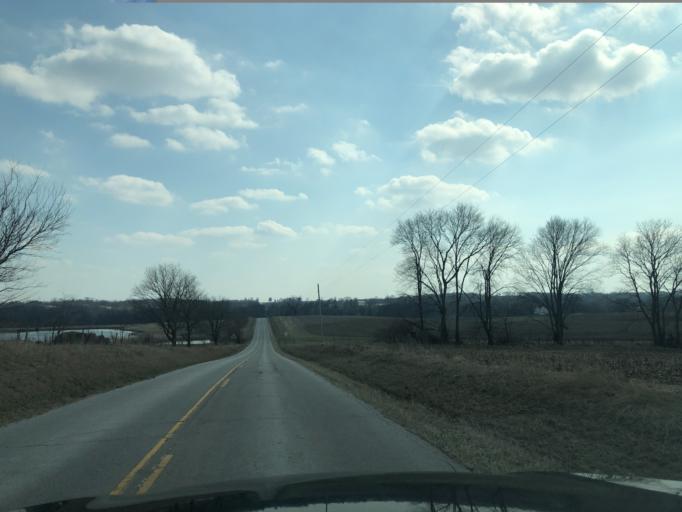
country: US
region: Missouri
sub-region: Platte County
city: Weston
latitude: 39.4959
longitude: -94.8454
